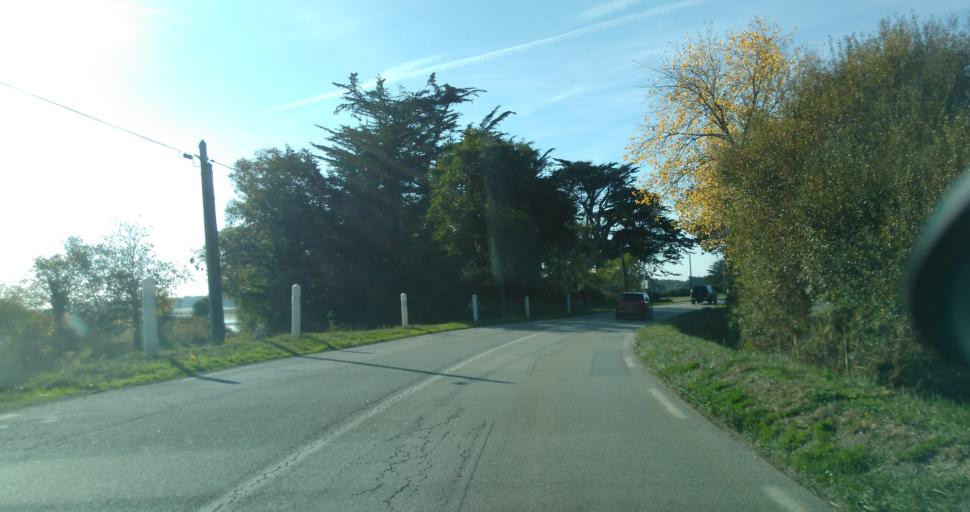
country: FR
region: Brittany
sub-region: Departement du Morbihan
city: Plouharnel
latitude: 47.5969
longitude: -3.1195
